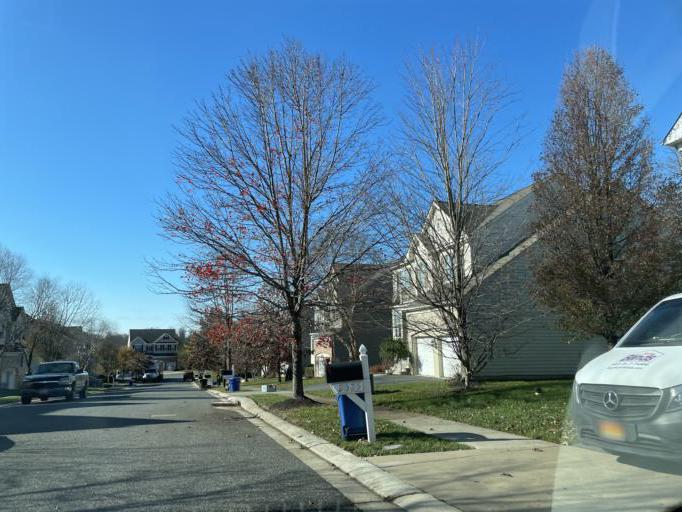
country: US
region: Maryland
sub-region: Baltimore County
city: Pikesville
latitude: 39.3756
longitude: -76.6647
